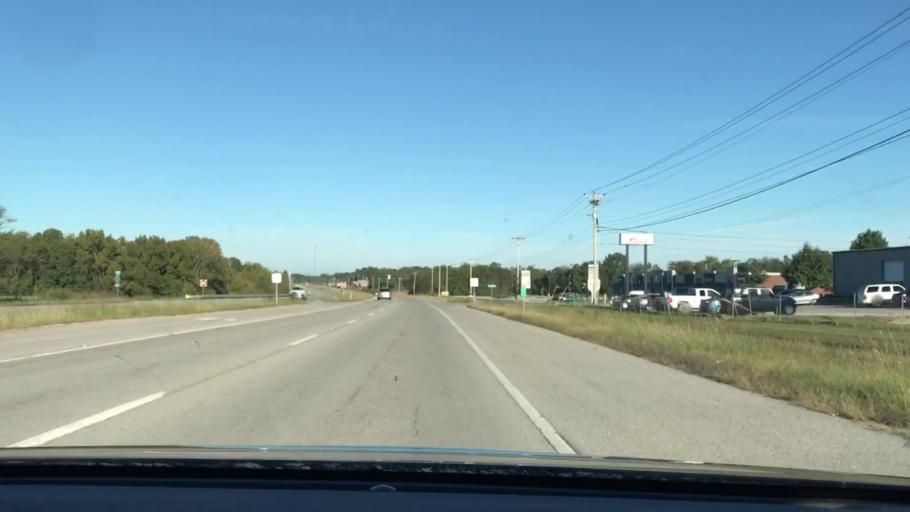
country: US
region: Kentucky
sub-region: Christian County
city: Hopkinsville
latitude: 36.8235
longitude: -87.5070
